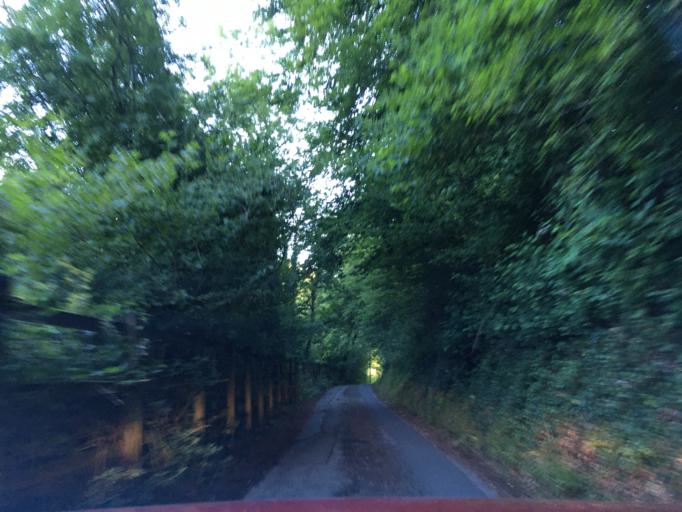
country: GB
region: Wales
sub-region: Monmouthshire
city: Tintern
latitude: 51.6992
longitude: -2.7121
